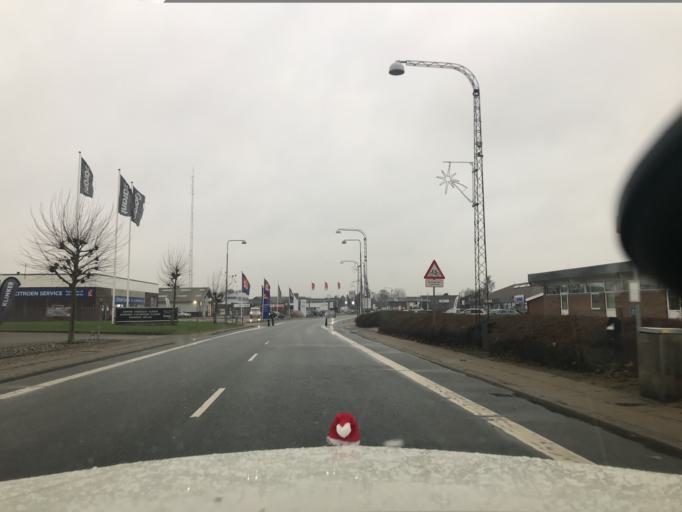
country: DK
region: South Denmark
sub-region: Aabenraa Kommune
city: Rodekro
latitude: 55.0697
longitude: 9.3509
